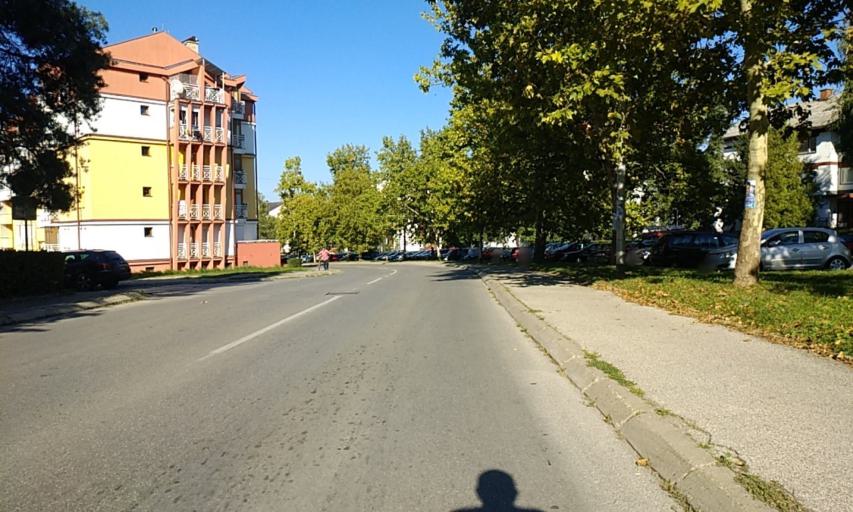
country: BA
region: Republika Srpska
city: Starcevica
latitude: 44.7569
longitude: 17.2108
